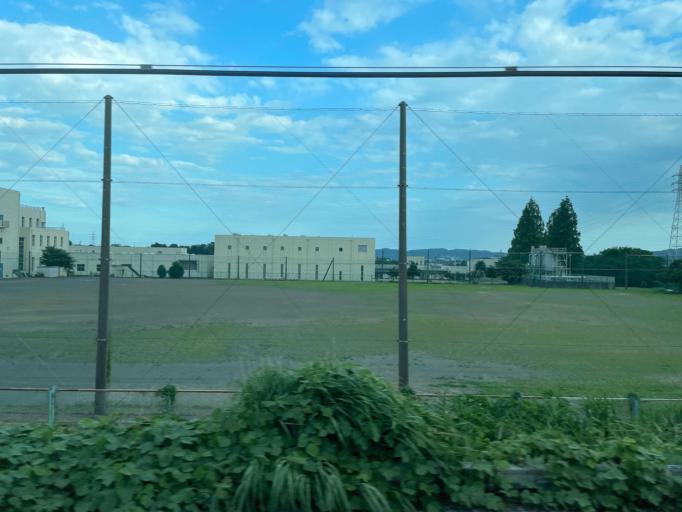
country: JP
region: Kanagawa
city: Isehara
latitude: 35.3872
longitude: 139.2943
